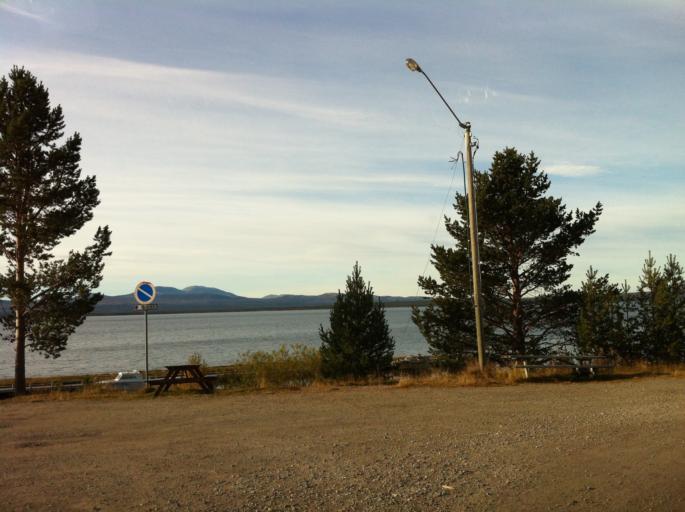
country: NO
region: Hedmark
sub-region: Engerdal
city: Engerdal
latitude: 62.1568
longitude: 11.9481
